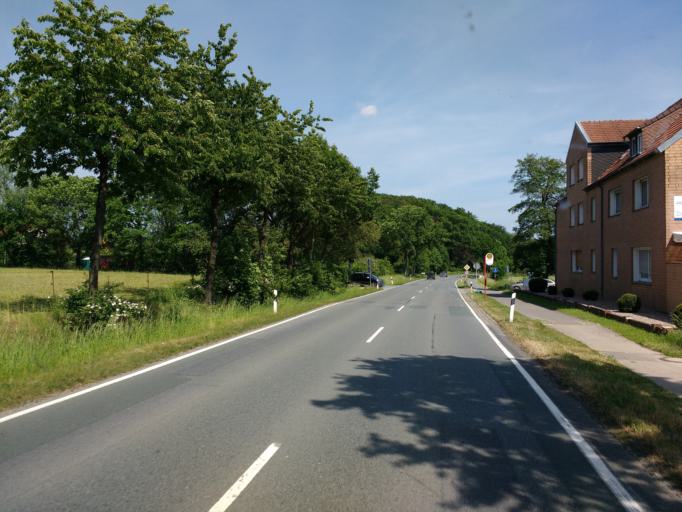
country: DE
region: Lower Saxony
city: Belm
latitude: 52.3090
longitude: 8.1141
